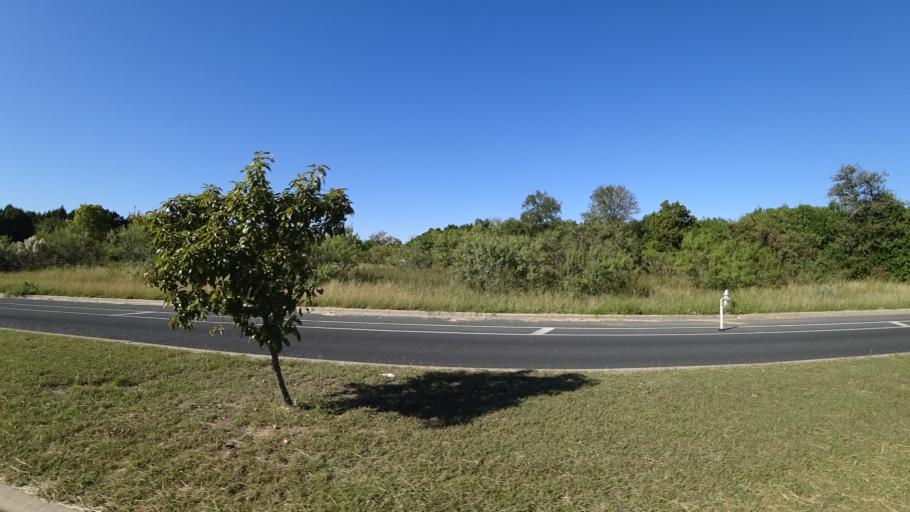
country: US
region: Texas
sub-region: Travis County
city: Austin
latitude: 30.2938
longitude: -97.6723
